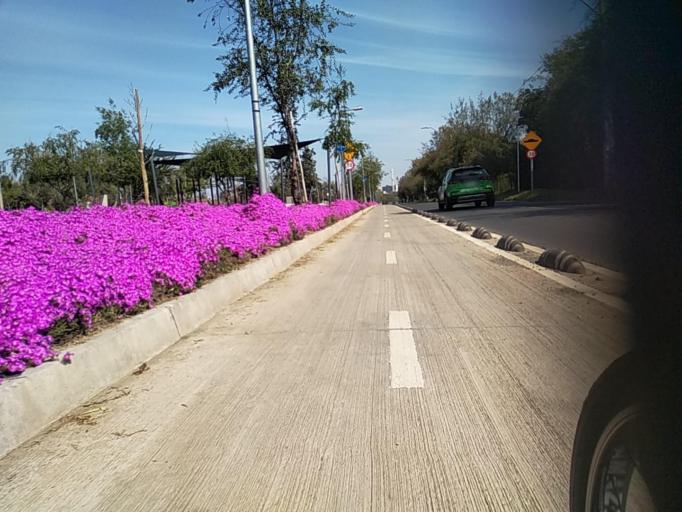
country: CL
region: Santiago Metropolitan
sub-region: Provincia de Santiago
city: Villa Presidente Frei, Nunoa, Santiago, Chile
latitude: -33.4992
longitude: -70.6058
